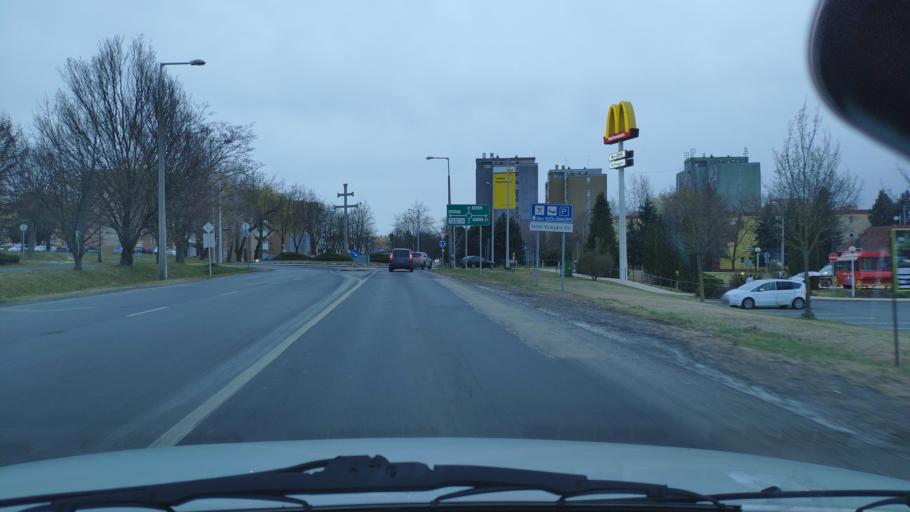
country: HU
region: Zala
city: Nagykanizsa
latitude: 46.4622
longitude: 17.0089
